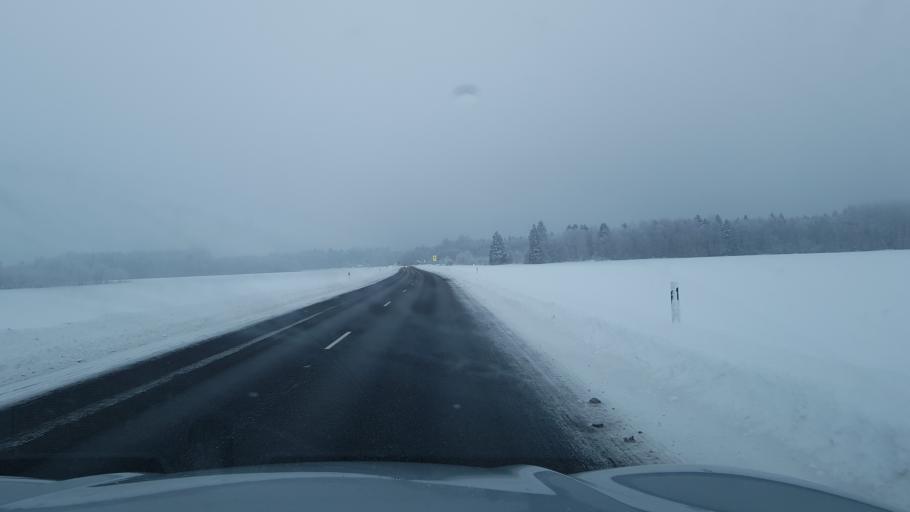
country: EE
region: Ida-Virumaa
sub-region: Johvi vald
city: Johvi
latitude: 59.3144
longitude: 27.3924
